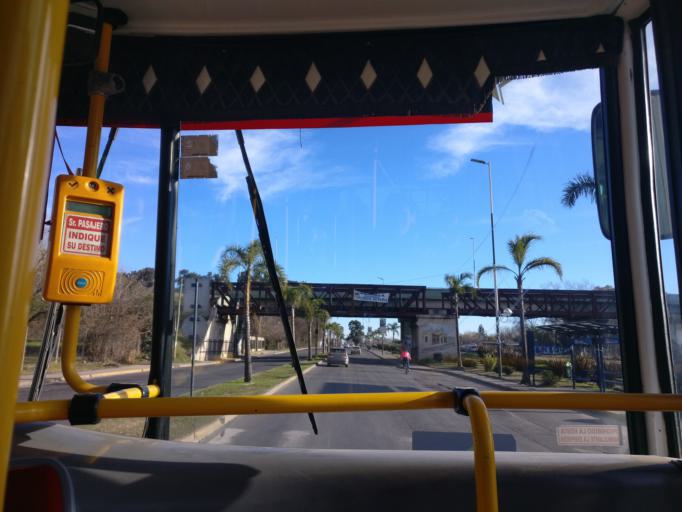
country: AR
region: Buenos Aires
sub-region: Partido de Ezeiza
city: Ezeiza
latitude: -34.8611
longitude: -58.5314
